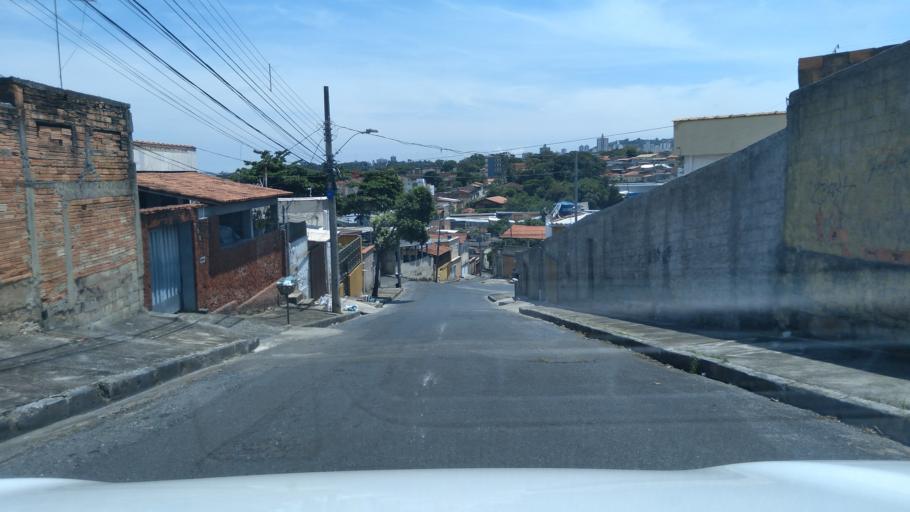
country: BR
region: Minas Gerais
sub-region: Contagem
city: Contagem
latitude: -19.9001
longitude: -44.0117
